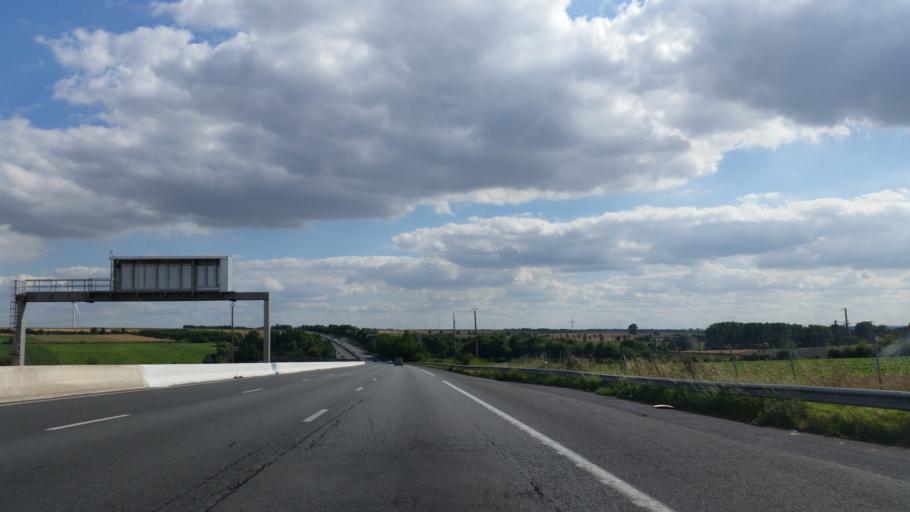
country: FR
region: Nord-Pas-de-Calais
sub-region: Departement du Pas-de-Calais
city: Croisilles
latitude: 50.2399
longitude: 2.8546
